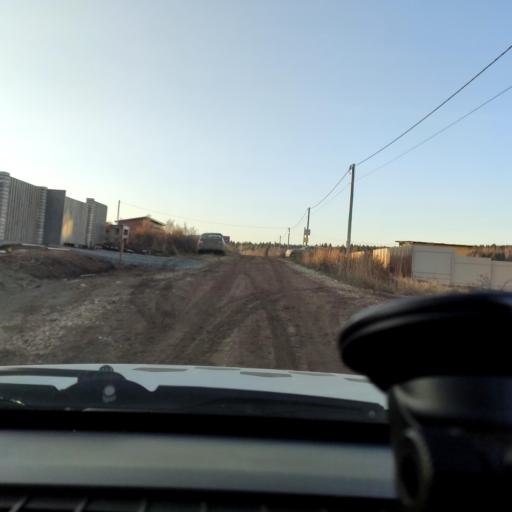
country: RU
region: Perm
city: Ferma
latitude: 57.9468
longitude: 56.3507
